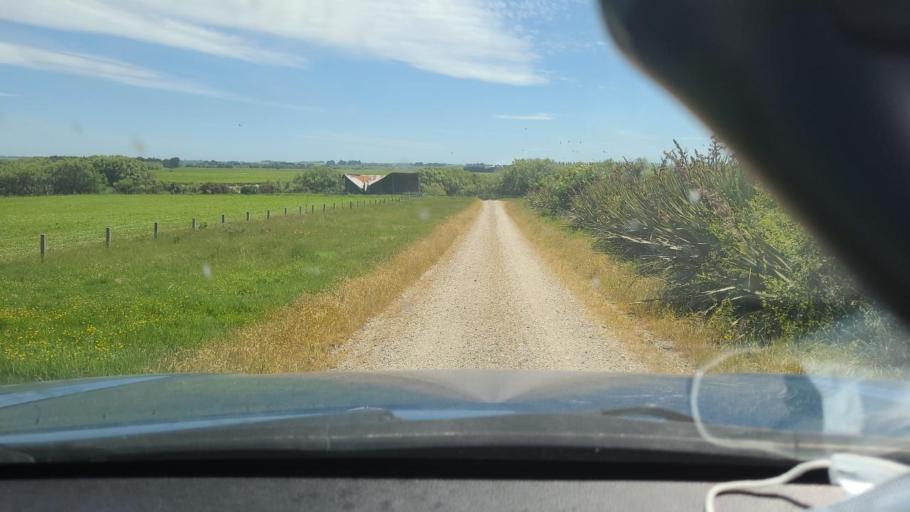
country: NZ
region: Southland
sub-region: Gore District
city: Gore
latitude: -46.3823
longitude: 168.8202
